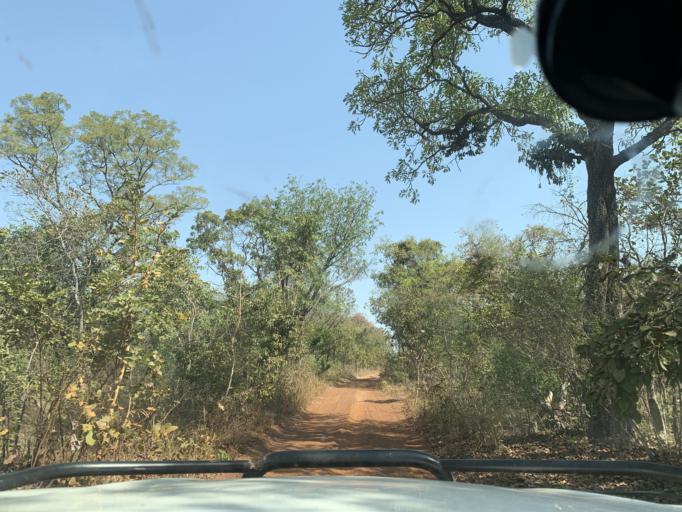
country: ML
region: Sikasso
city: Kolondieba
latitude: 10.8868
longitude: -6.7601
